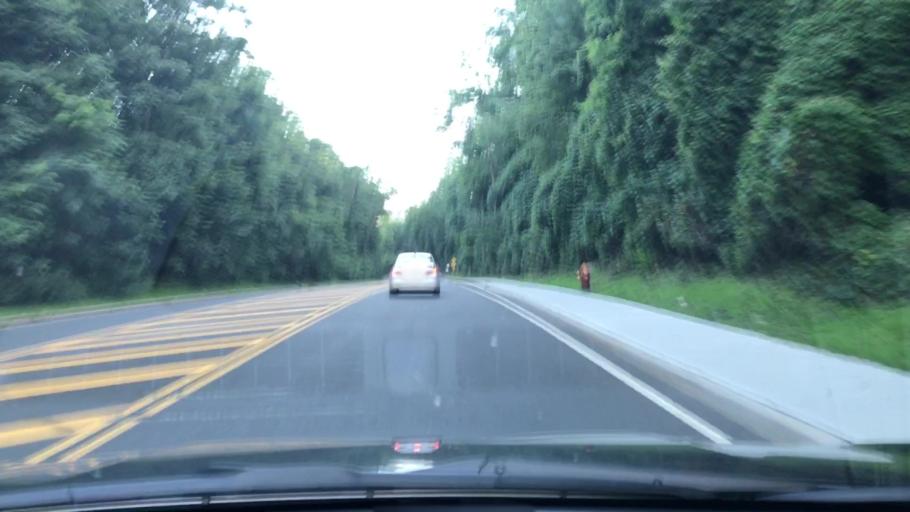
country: US
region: New York
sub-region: Westchester County
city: Hastings-on-Hudson
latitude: 40.9726
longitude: -73.8757
